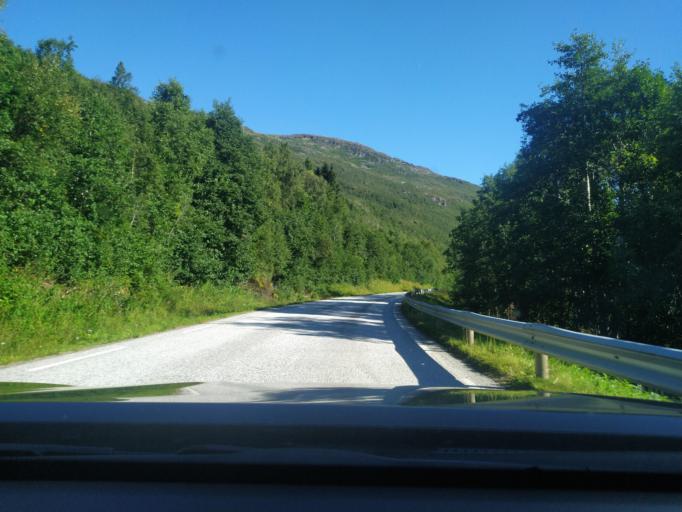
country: NO
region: Troms
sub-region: Dyroy
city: Brostadbotn
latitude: 68.9265
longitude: 17.6405
